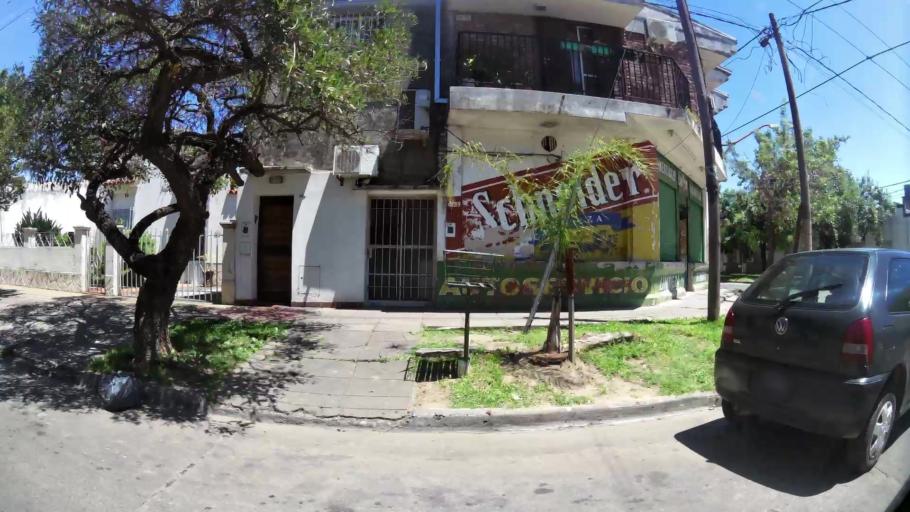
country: AR
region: Santa Fe
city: Santa Fe de la Vera Cruz
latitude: -31.6270
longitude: -60.7119
